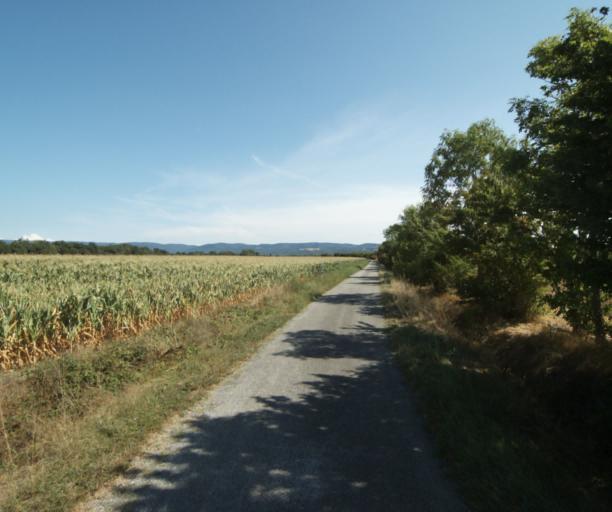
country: FR
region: Midi-Pyrenees
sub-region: Departement de la Haute-Garonne
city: Revel
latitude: 43.4885
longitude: 1.9723
